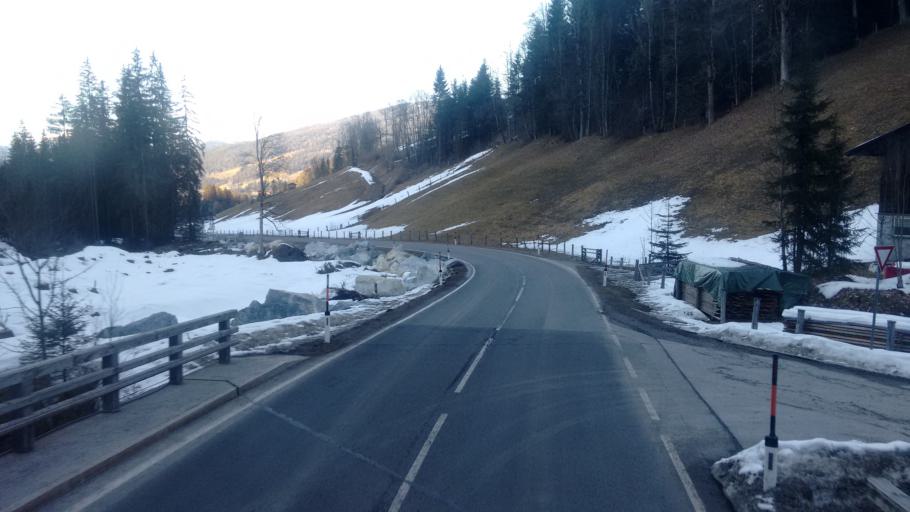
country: AT
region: Salzburg
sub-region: Politischer Bezirk Sankt Johann im Pongau
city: Altenmarkt im Pongau
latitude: 47.3531
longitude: 13.4286
